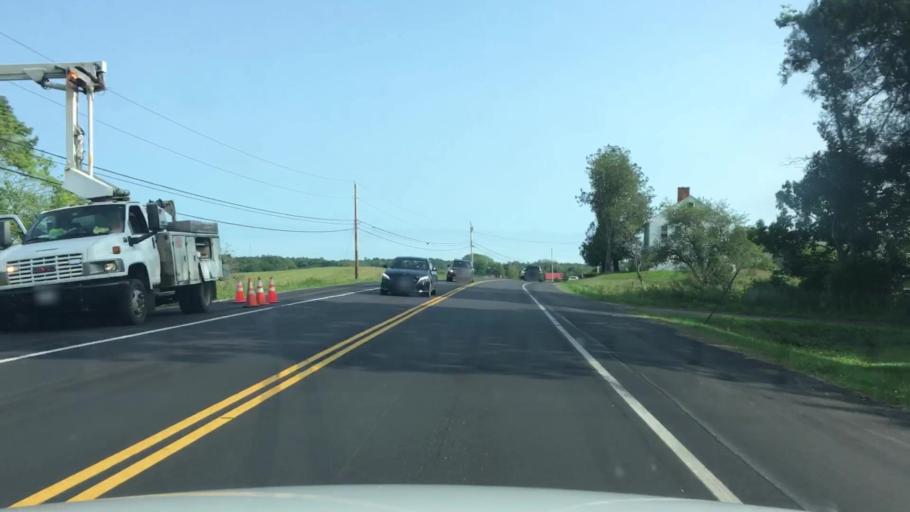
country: US
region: Maine
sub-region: Knox County
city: Warren
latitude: 44.1052
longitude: -69.2510
